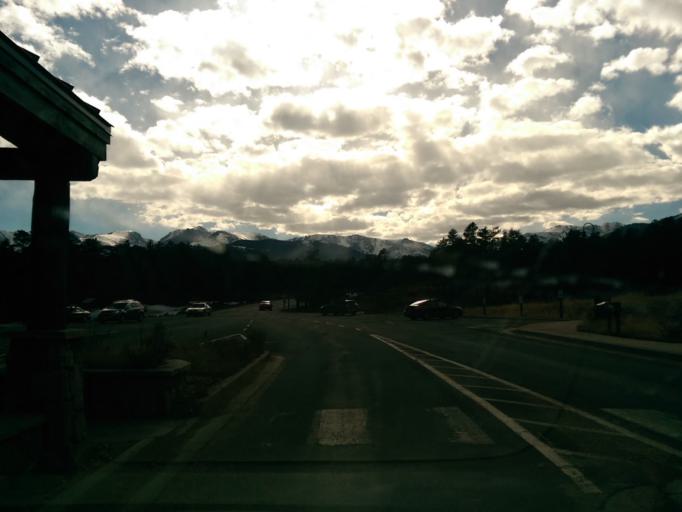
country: US
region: Colorado
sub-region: Larimer County
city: Estes Park
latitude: 40.3665
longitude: -105.5811
